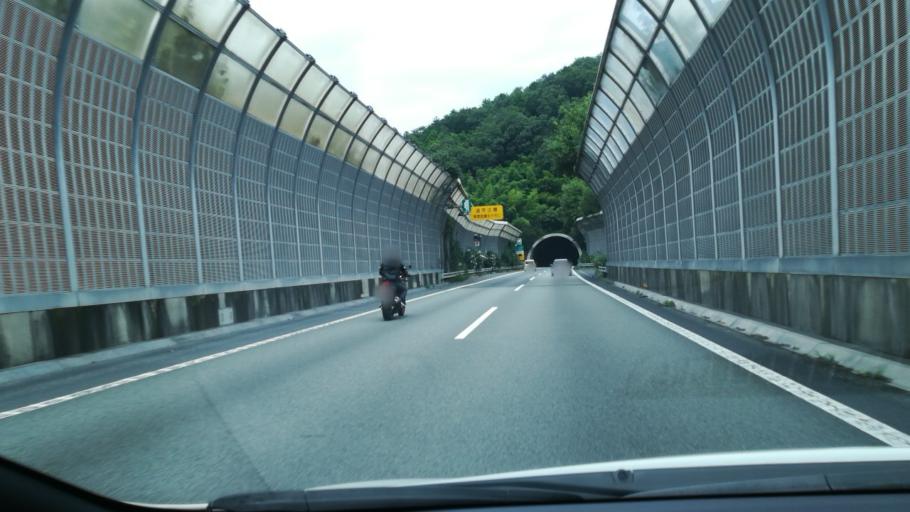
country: JP
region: Tokyo
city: Fussa
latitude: 35.7426
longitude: 139.2814
